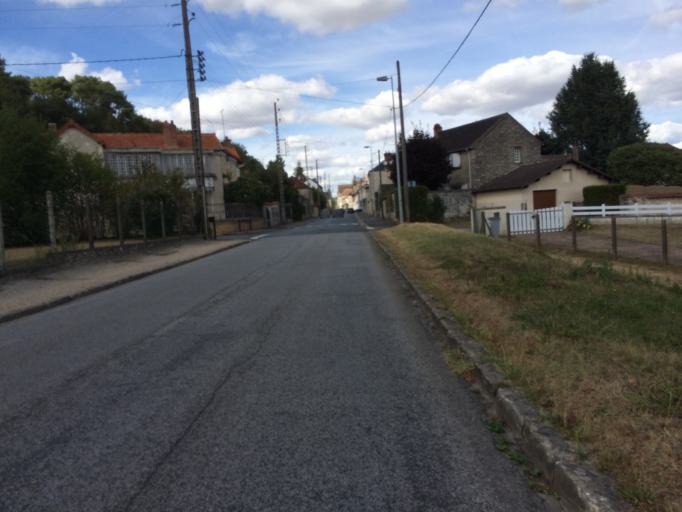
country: FR
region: Ile-de-France
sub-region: Departement de l'Essonne
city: Maisse
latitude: 48.3913
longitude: 2.3752
